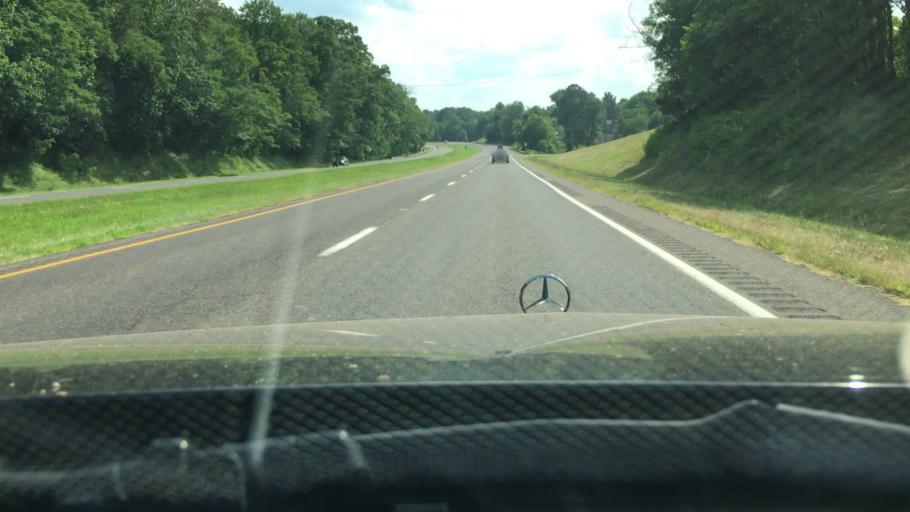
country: US
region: Virginia
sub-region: Orange County
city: Gordonsville
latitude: 38.1734
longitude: -78.1549
